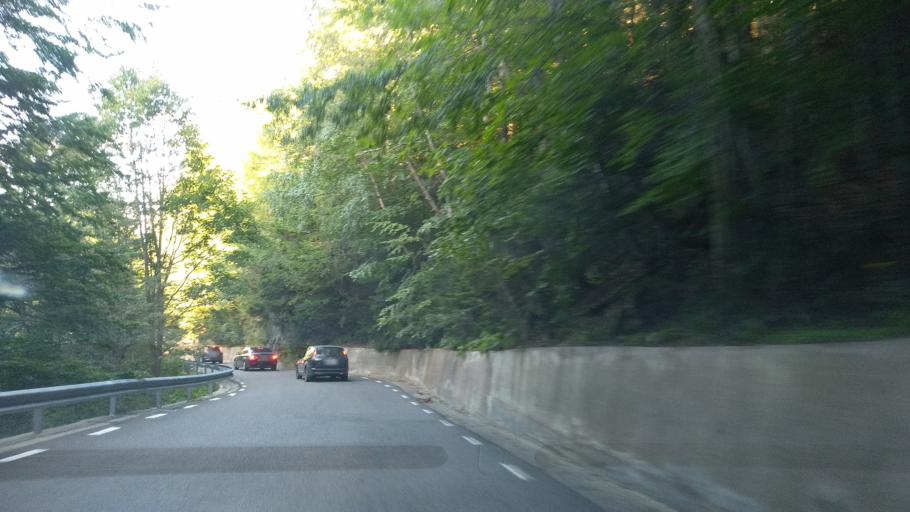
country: RO
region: Prahova
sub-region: Oras Sinaia
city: Sinaia
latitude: 45.3225
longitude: 25.4992
